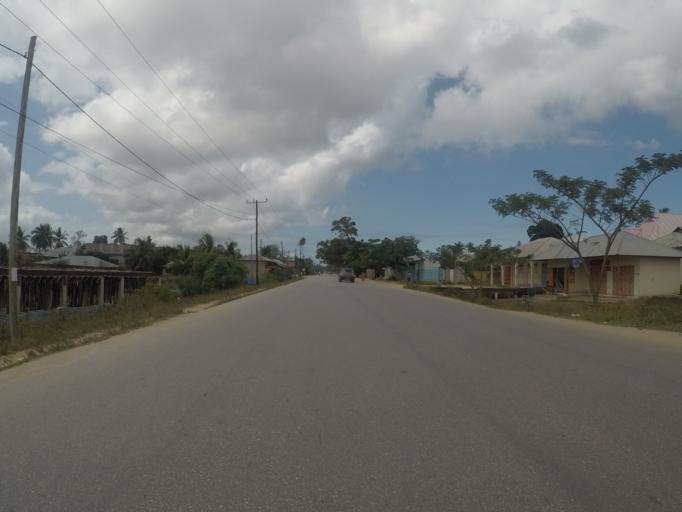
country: TZ
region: Zanzibar Urban/West
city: Zanzibar
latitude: -6.2038
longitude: 39.2270
